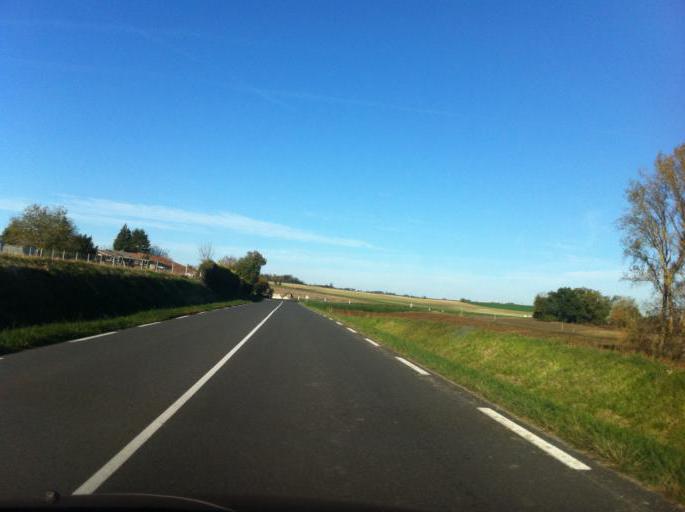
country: FR
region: Aquitaine
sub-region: Departement de la Dordogne
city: Saint-Aulaye
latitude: 45.2743
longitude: 0.1493
